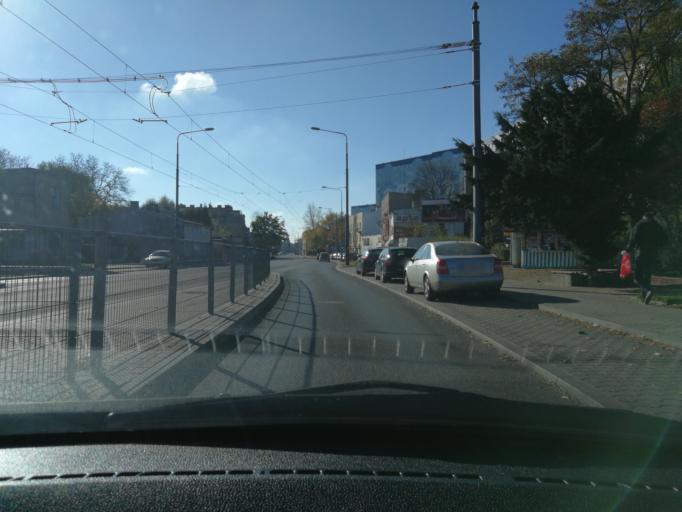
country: PL
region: Lodz Voivodeship
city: Lodz
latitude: 51.7991
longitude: 19.4562
